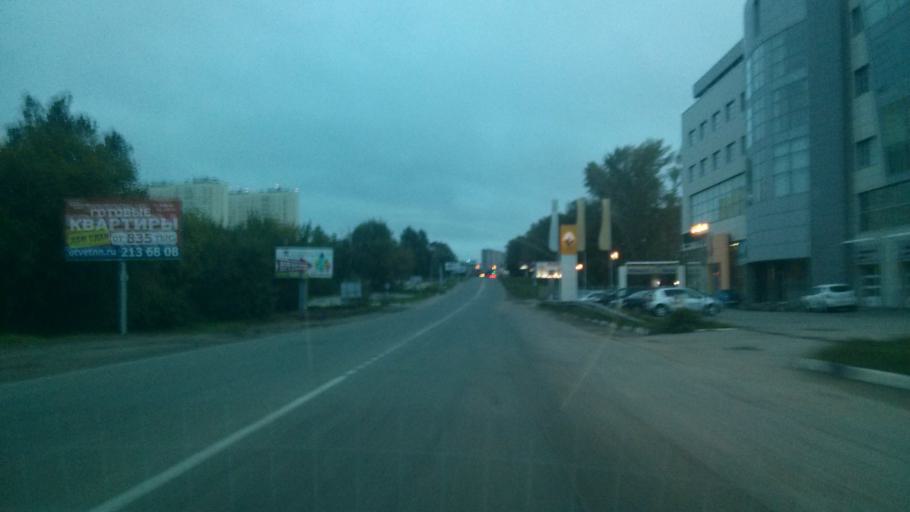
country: RU
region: Nizjnij Novgorod
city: Afonino
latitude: 56.2806
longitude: 44.0809
